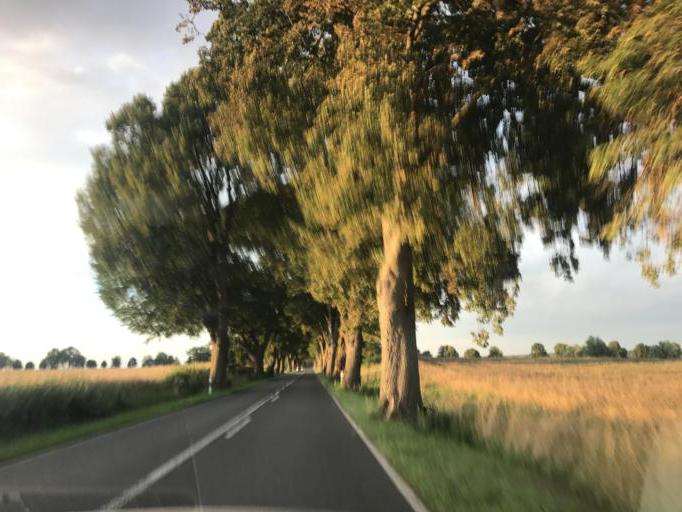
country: DE
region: Mecklenburg-Vorpommern
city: Wesenberg
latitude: 53.3275
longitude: 12.8771
